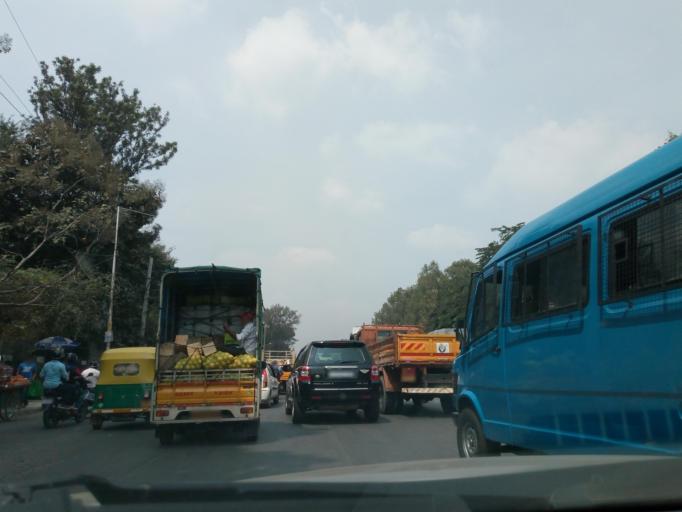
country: IN
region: Karnataka
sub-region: Bangalore Urban
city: Bangalore
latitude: 12.9280
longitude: 77.6159
